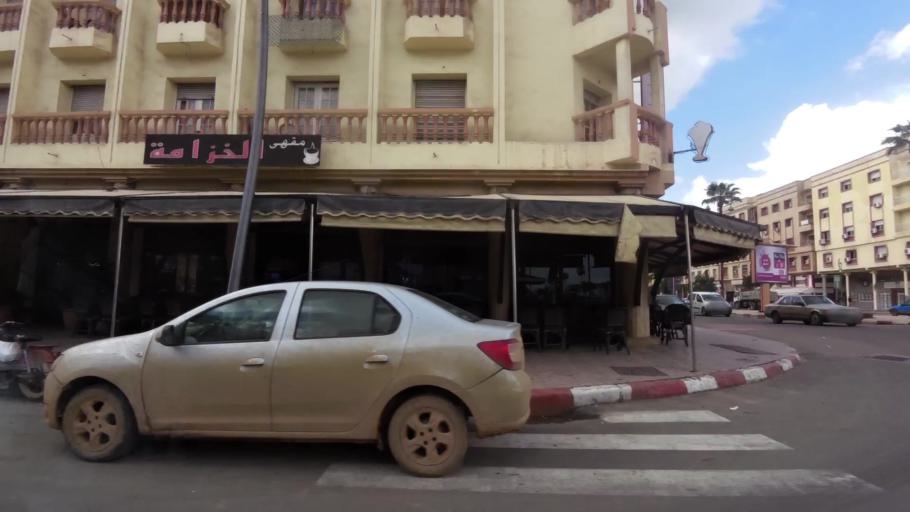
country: MA
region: Chaouia-Ouardigha
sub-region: Settat Province
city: Berrechid
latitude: 33.2716
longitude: -7.5864
